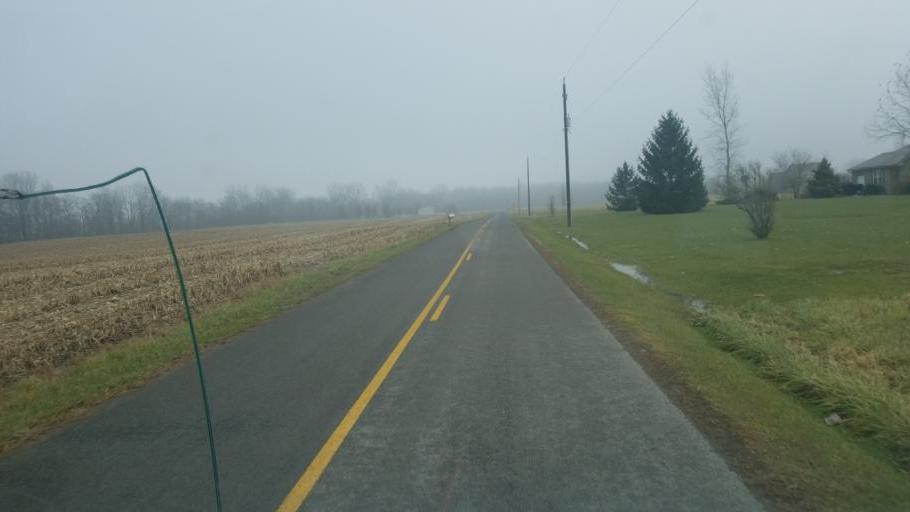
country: US
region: Ohio
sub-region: Hardin County
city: Kenton
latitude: 40.5032
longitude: -83.5251
